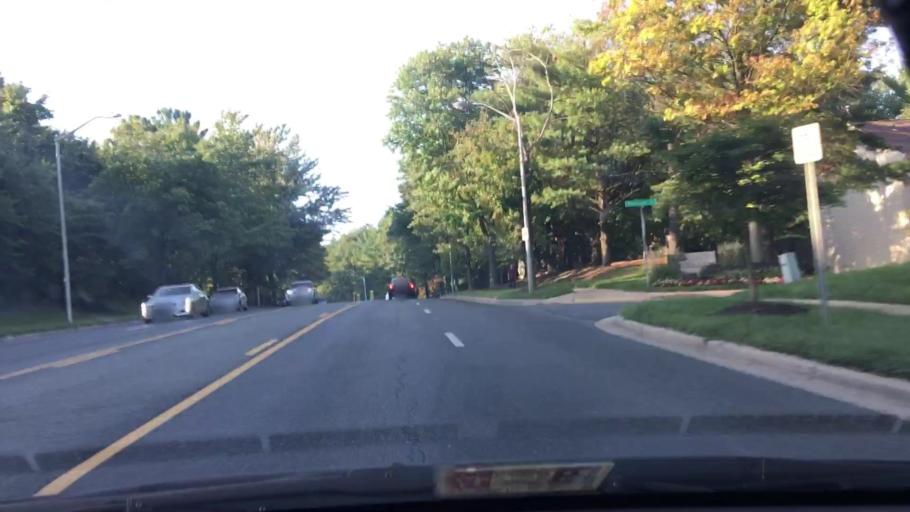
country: US
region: Maryland
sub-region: Montgomery County
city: Derwood
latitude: 39.1184
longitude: -77.1569
